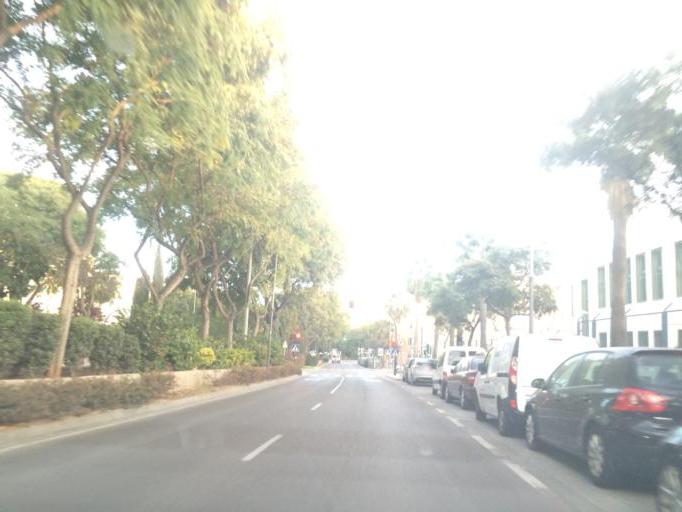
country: ES
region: Andalusia
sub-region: Provincia de Almeria
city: Almeria
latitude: 36.8486
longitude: -2.4623
